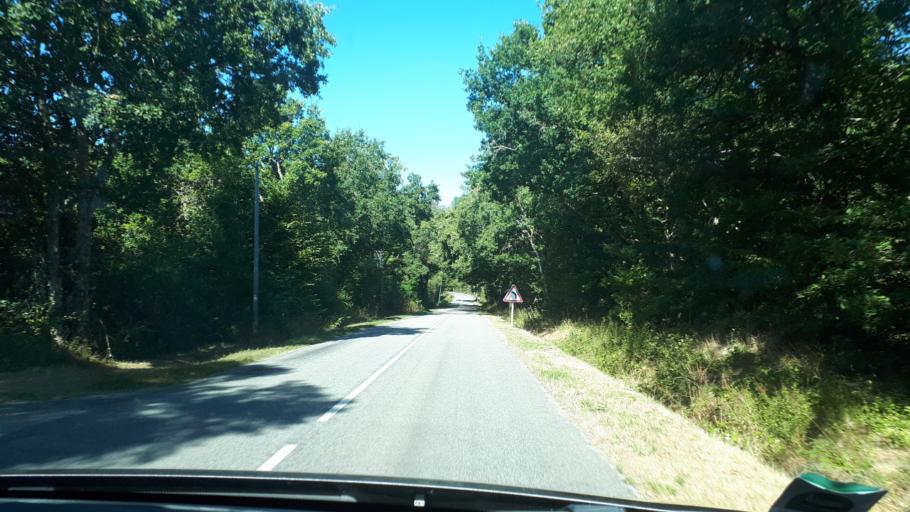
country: FR
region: Centre
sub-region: Departement du Loiret
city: Saint-Brisson-sur-Loire
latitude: 47.5959
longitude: 2.6903
